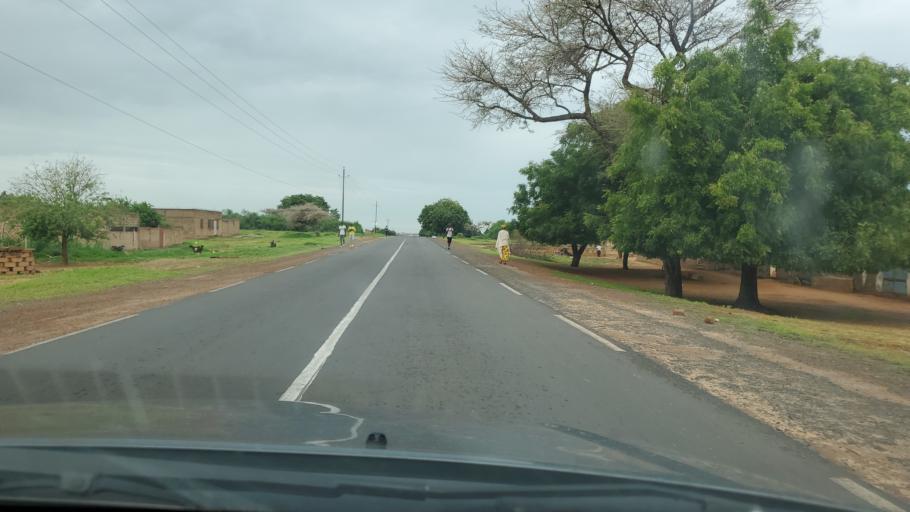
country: SN
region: Thies
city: Mekhe
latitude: 15.1334
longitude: -16.8570
